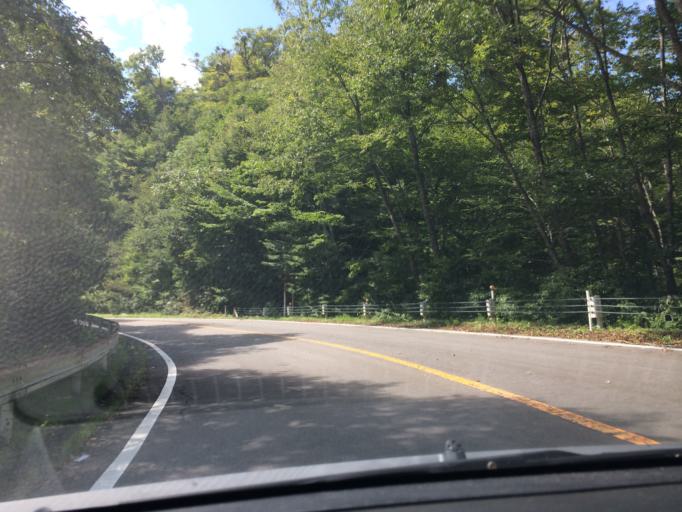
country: JP
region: Tottori
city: Kurayoshi
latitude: 35.3289
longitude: 133.5975
